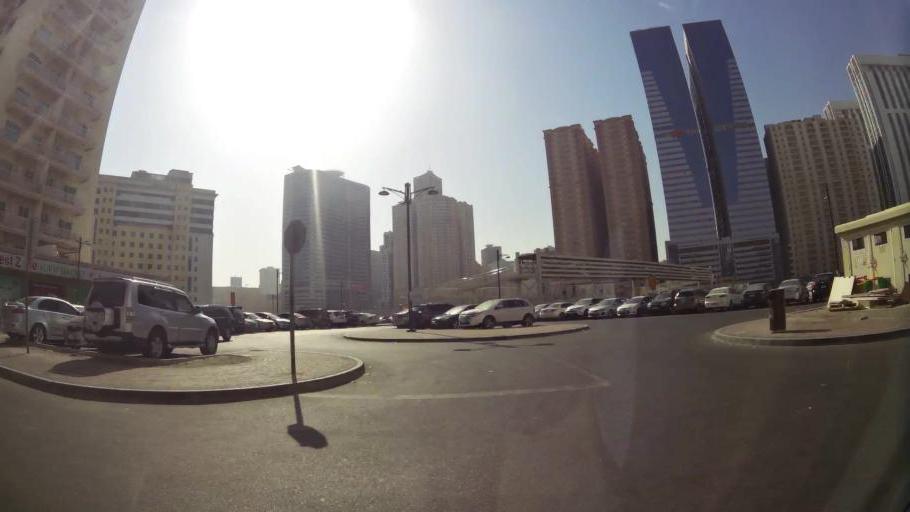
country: AE
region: Ash Shariqah
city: Sharjah
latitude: 25.2977
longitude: 55.3808
